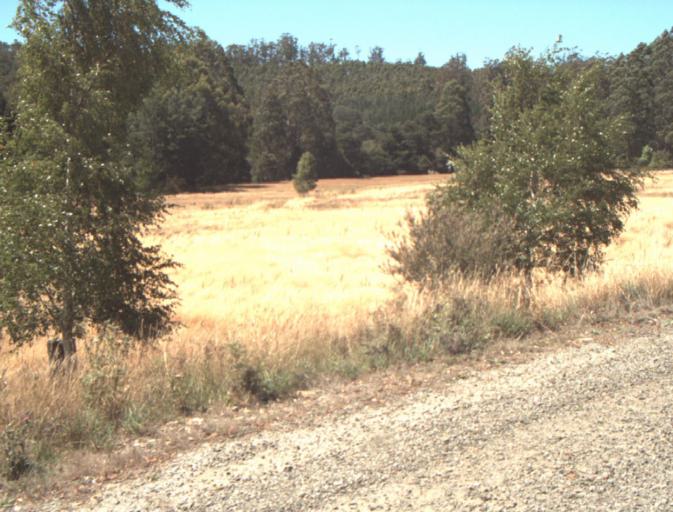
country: AU
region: Tasmania
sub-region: Dorset
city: Scottsdale
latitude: -41.2943
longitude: 147.4038
